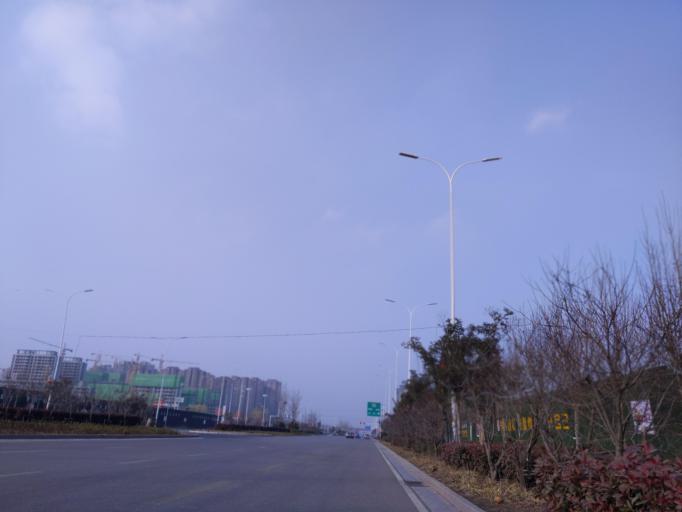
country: CN
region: Henan Sheng
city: Puyang
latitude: 35.8079
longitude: 115.0222
